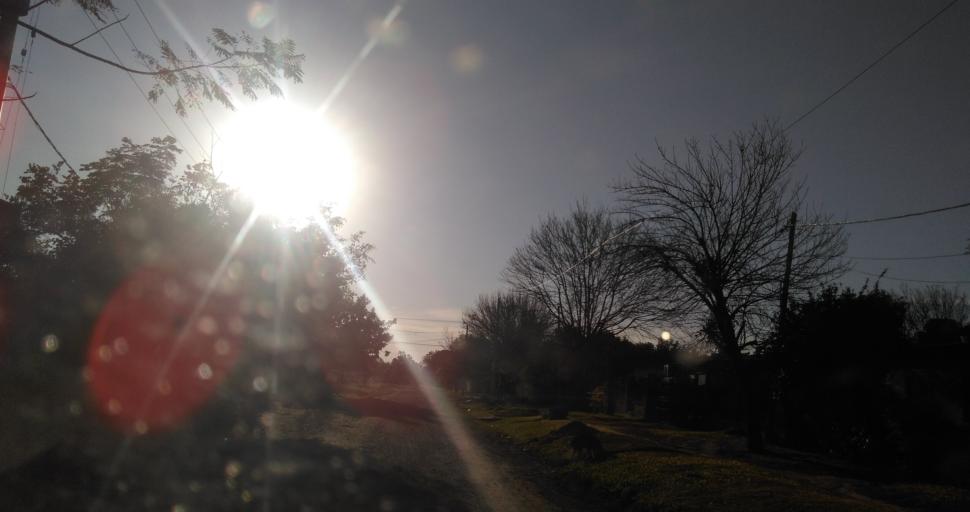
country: AR
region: Chaco
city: Colonia Benitez
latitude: -27.3334
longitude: -58.9423
